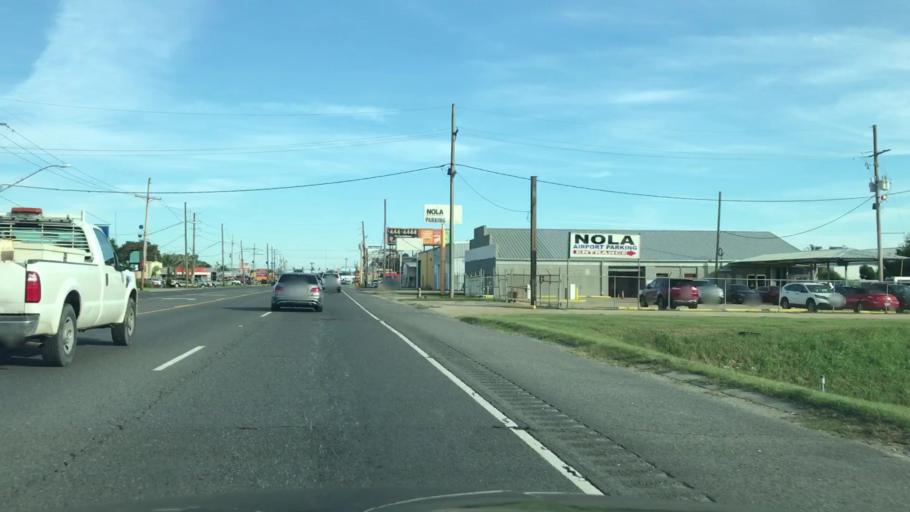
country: US
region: Louisiana
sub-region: Jefferson Parish
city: Kenner
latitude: 29.9810
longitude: -90.2509
